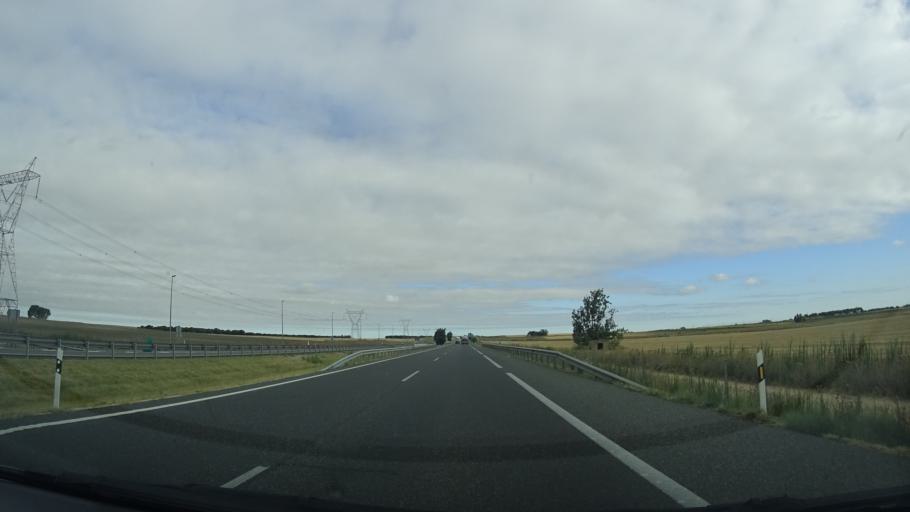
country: ES
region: Castille and Leon
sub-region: Provincia de Avila
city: Palacios de Goda
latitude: 41.1344
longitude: -4.7775
